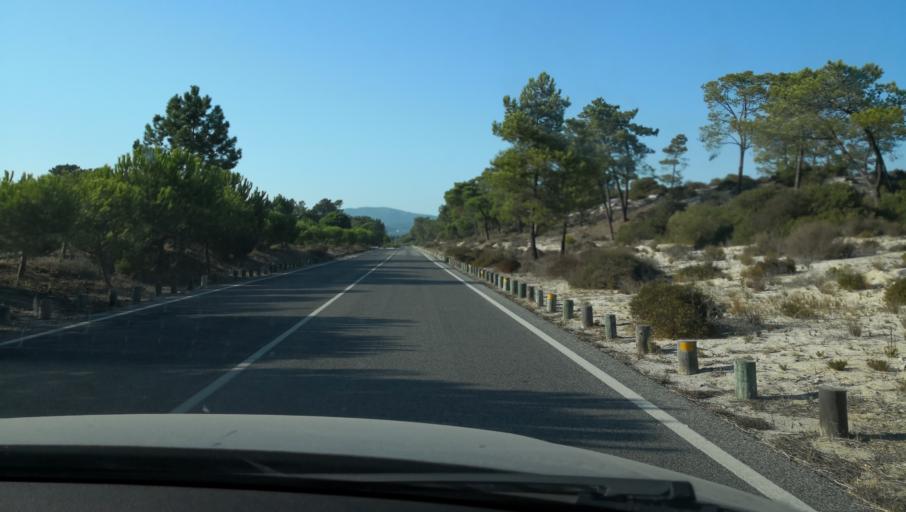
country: PT
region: Setubal
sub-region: Setubal
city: Setubal
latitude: 38.4800
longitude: -8.8901
